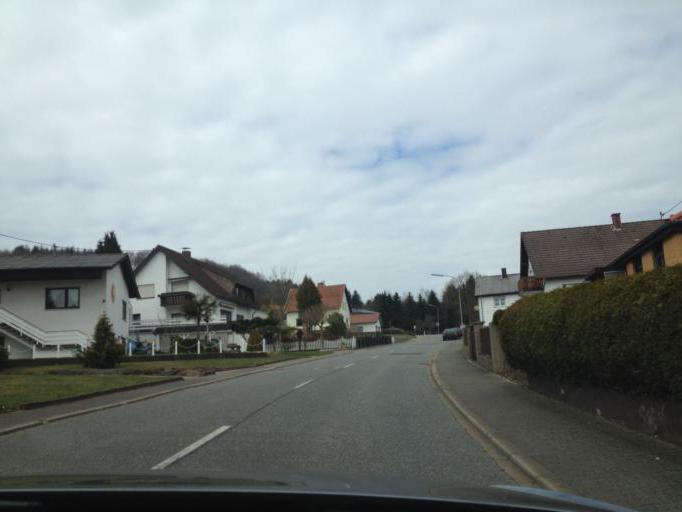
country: DE
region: Saarland
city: Freisen
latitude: 49.5563
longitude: 7.2453
